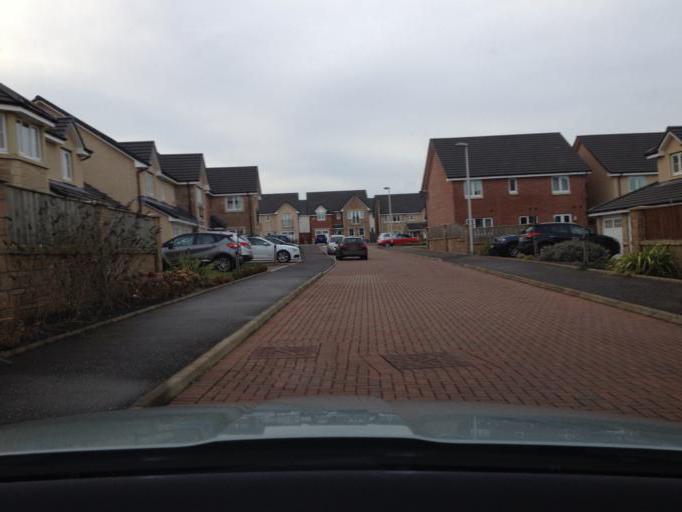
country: GB
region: Scotland
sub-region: Edinburgh
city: Kirkliston
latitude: 55.9596
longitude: -3.3978
